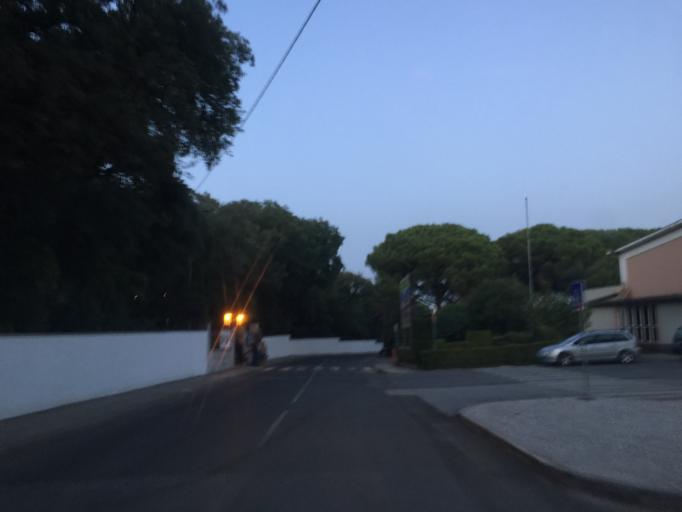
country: PT
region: Leiria
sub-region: Bombarral
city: Bombarral
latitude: 39.2664
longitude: -9.1571
